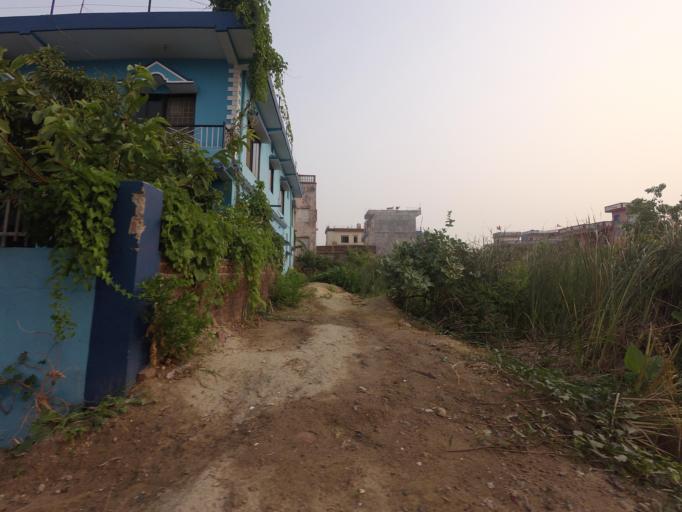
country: NP
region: Western Region
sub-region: Lumbini Zone
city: Bhairahawa
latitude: 27.5122
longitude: 83.4465
